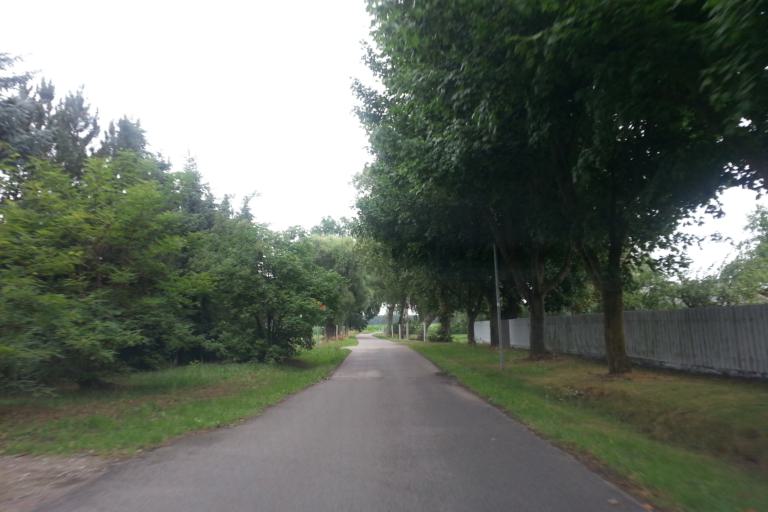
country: DE
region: Mecklenburg-Vorpommern
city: Ferdinandshof
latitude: 53.6896
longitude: 13.9009
